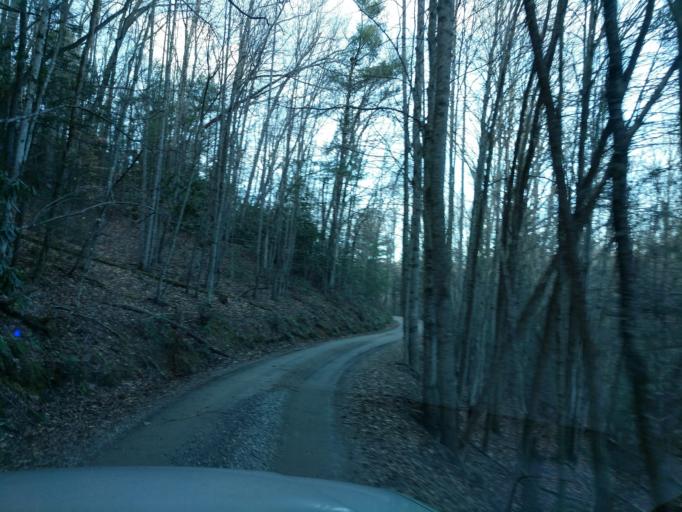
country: US
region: North Carolina
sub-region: Haywood County
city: Cove Creek
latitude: 35.7334
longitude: -83.0349
